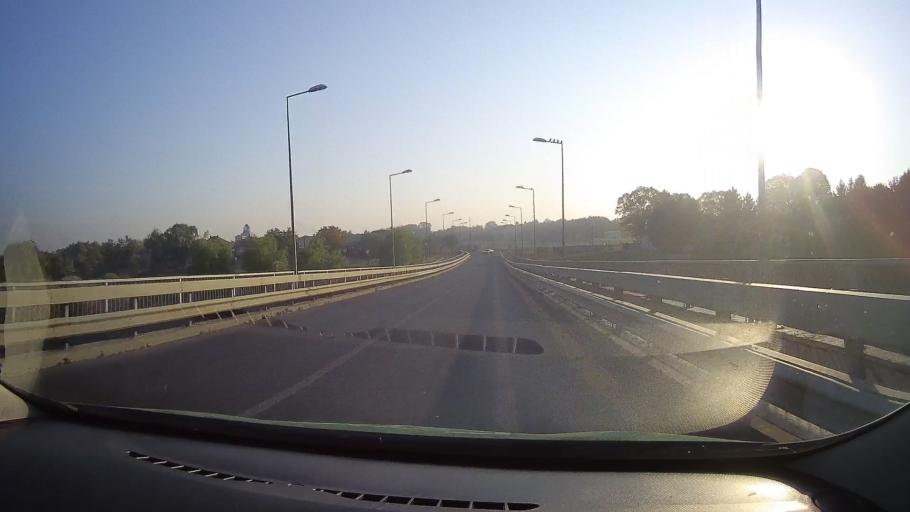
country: RO
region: Arad
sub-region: Comuna Curtici
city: Curtici
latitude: 46.3380
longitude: 21.3011
